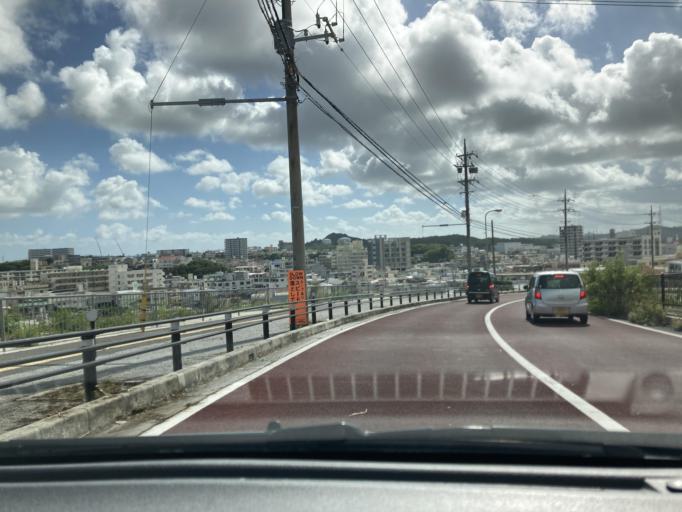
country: JP
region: Okinawa
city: Tomigusuku
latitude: 26.1992
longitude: 127.7295
